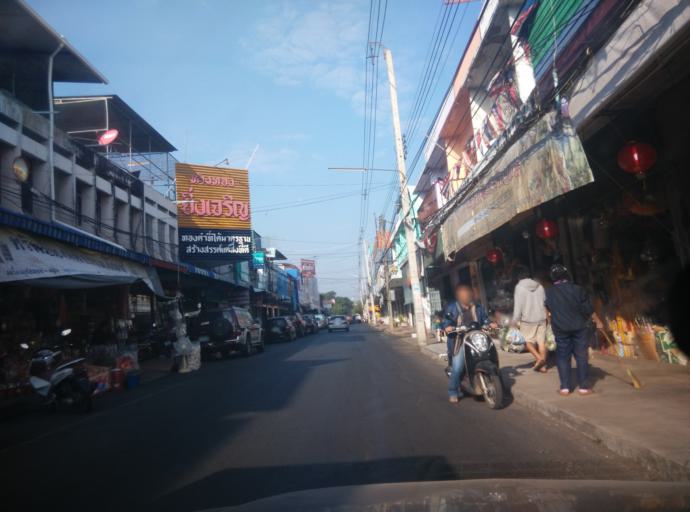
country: TH
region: Sisaket
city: Si Sa Ket
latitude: 15.1165
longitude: 104.3294
